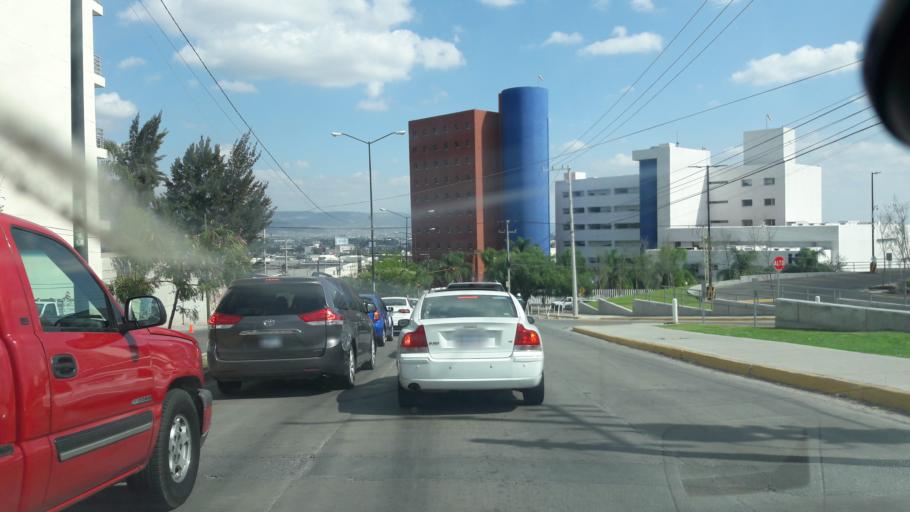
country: MX
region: Guanajuato
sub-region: Leon
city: La Ermita
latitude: 21.1581
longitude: -101.7025
